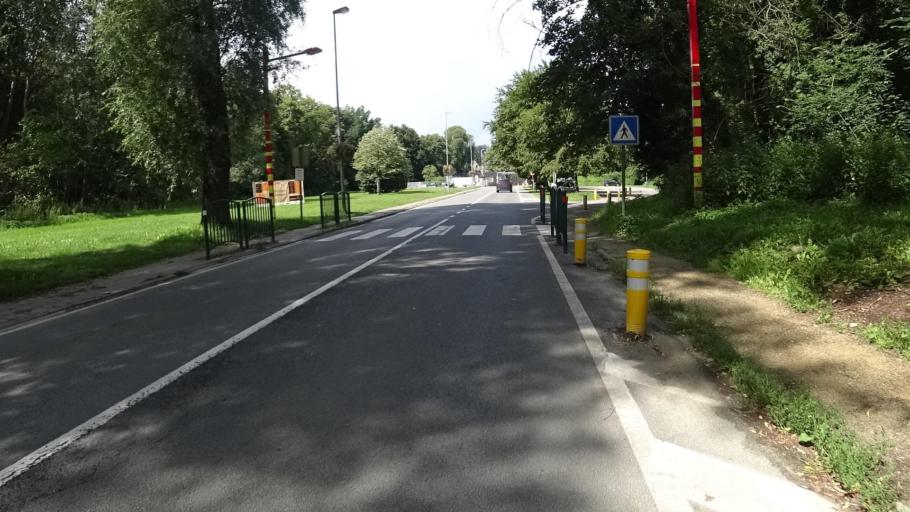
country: BE
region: Wallonia
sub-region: Province du Brabant Wallon
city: Villers-la-Ville
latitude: 50.5865
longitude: 4.5295
